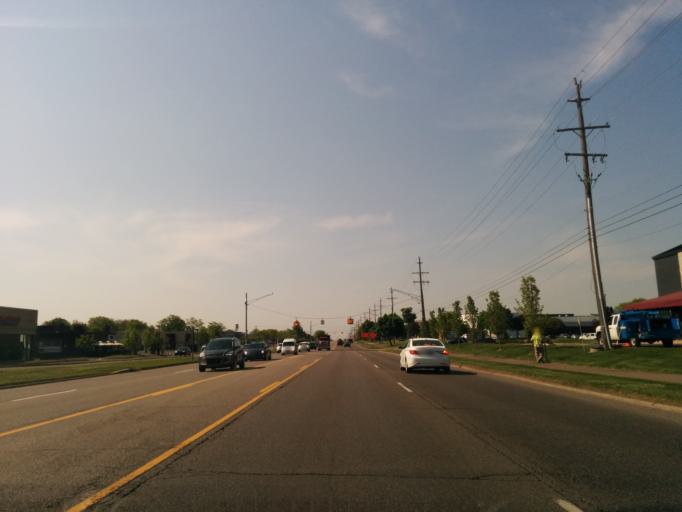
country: US
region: Michigan
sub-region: Oakland County
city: West Bloomfield Township
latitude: 42.5408
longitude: -83.3607
